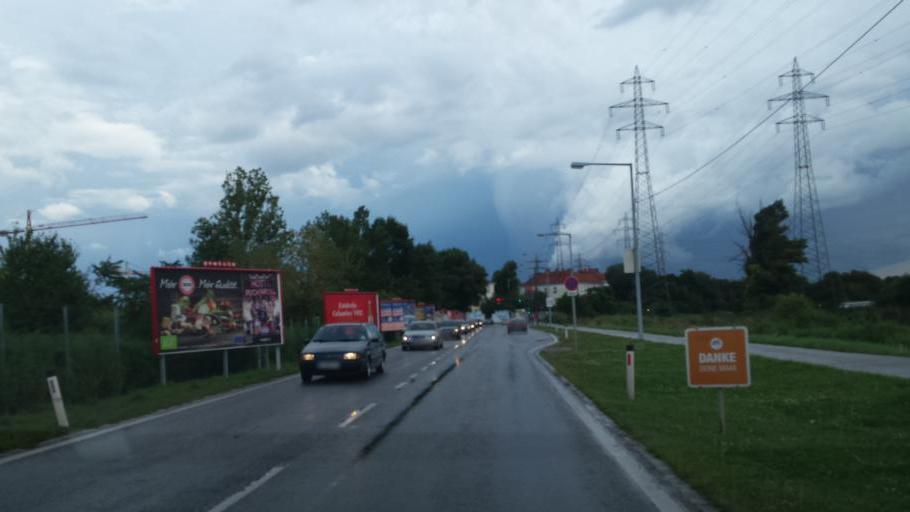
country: AT
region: Lower Austria
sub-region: Politischer Bezirk Wien-Umgebung
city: Schwechat
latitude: 48.1681
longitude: 16.4667
